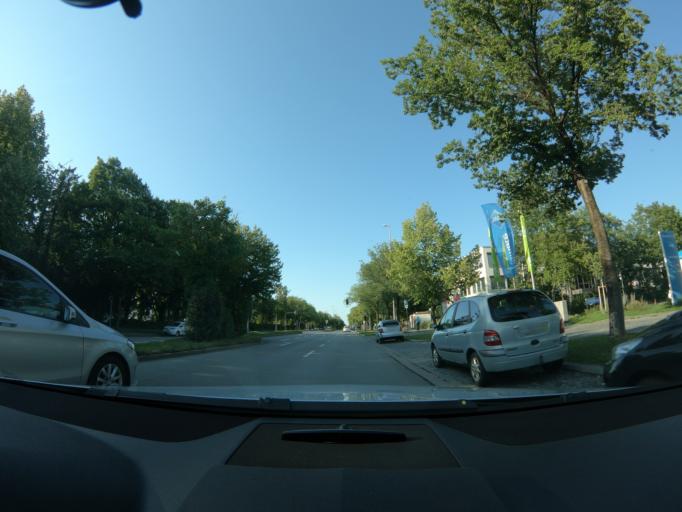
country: DE
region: Bavaria
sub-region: Upper Bavaria
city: Oberschleissheim
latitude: 48.2021
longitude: 11.5857
